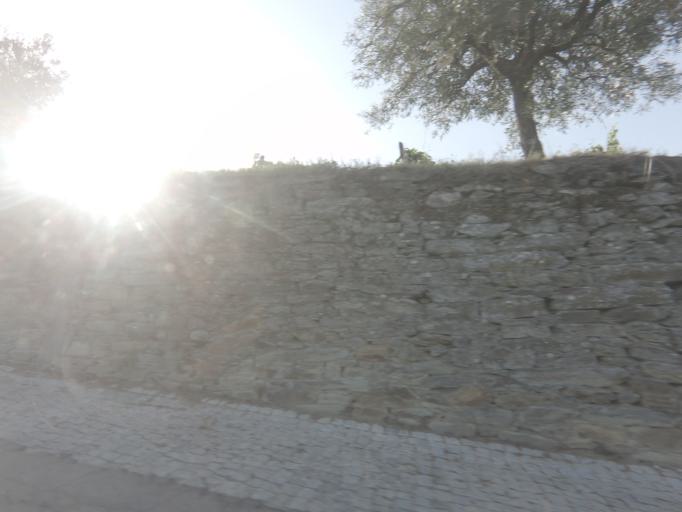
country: PT
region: Viseu
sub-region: Sao Joao da Pesqueira
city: Sao Joao da Pesqueira
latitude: 41.2249
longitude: -7.4665
